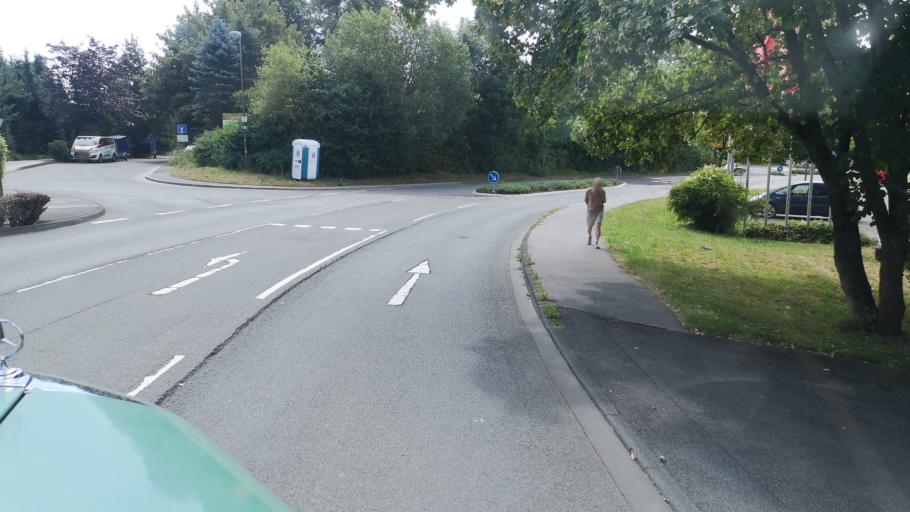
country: DE
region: North Rhine-Westphalia
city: Radevormwald
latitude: 51.1996
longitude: 7.3732
